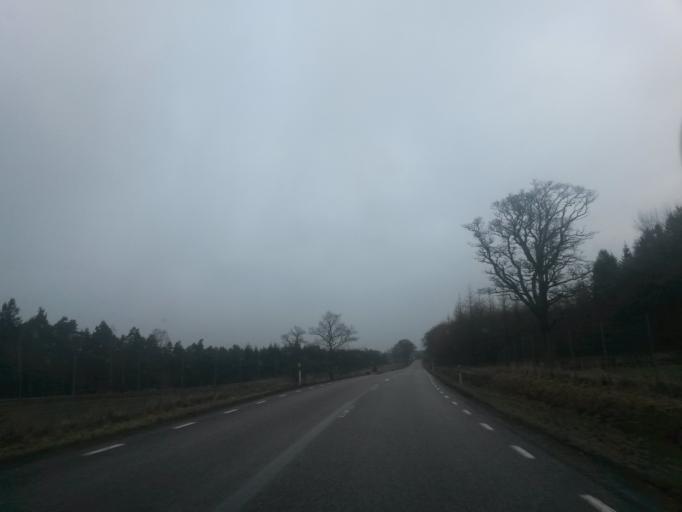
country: SE
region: Vaestra Goetaland
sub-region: Alingsas Kommun
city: Sollebrunn
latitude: 58.1511
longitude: 12.4182
